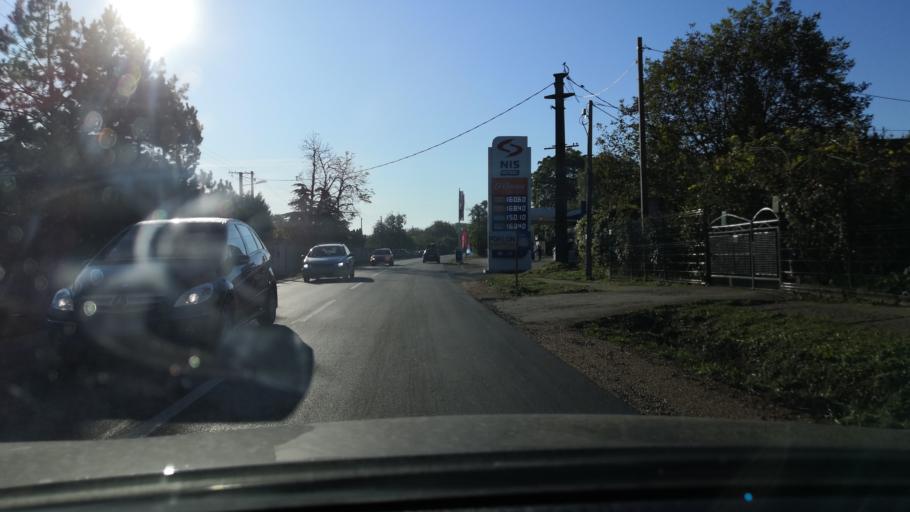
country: RS
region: Autonomna Pokrajina Vojvodina
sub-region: Juznobacki Okrug
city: Petrovaradin
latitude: 45.2320
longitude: 19.8928
